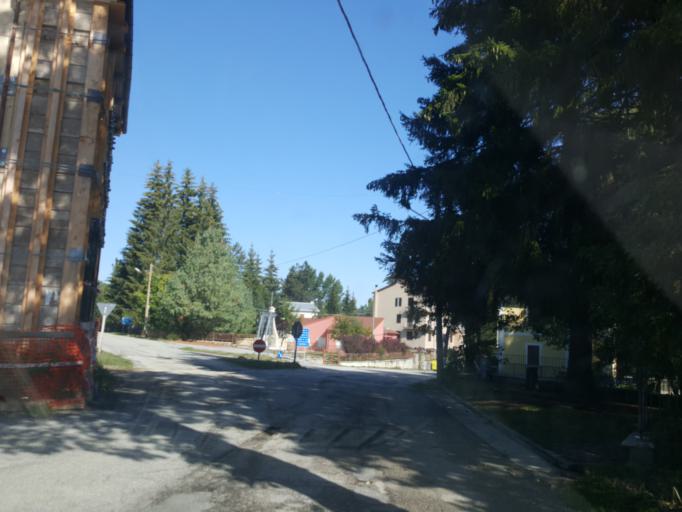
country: IT
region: Abruzzo
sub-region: Provincia dell' Aquila
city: Campotosto
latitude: 42.5609
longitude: 13.3267
